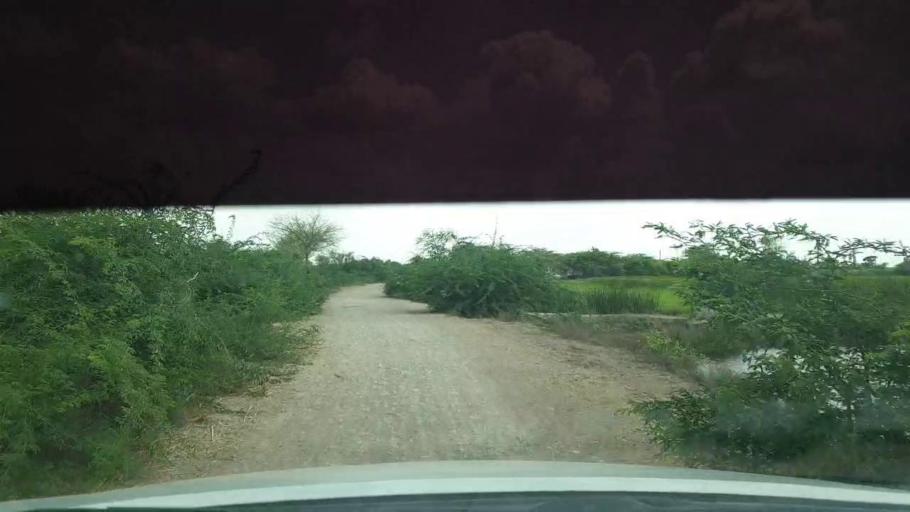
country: PK
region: Sindh
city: Kadhan
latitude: 24.6201
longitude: 69.0313
